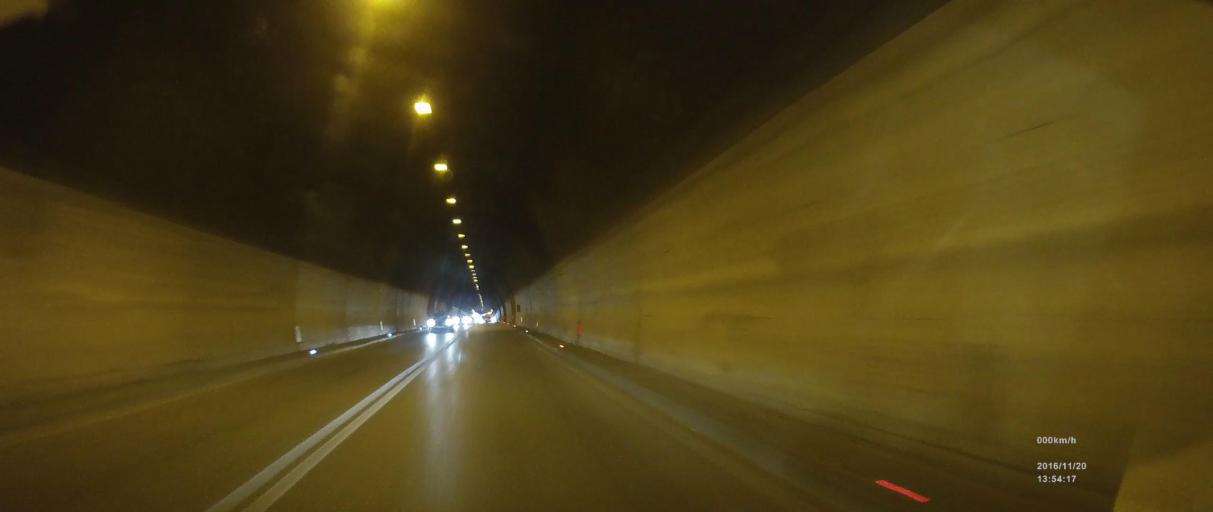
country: HR
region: Splitsko-Dalmatinska
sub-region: Grad Split
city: Split
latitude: 43.5093
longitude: 16.4259
